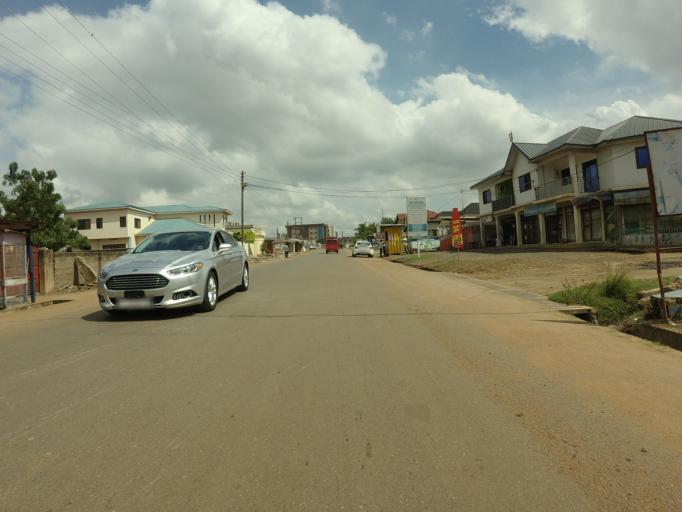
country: GH
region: Greater Accra
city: Nungua
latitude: 5.6272
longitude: -0.0927
